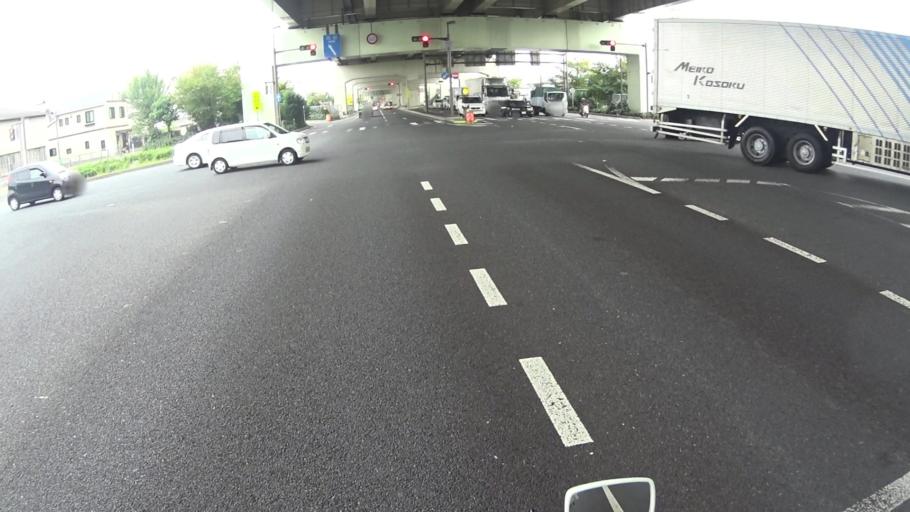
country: JP
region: Kyoto
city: Yawata
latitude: 34.8877
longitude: 135.7497
